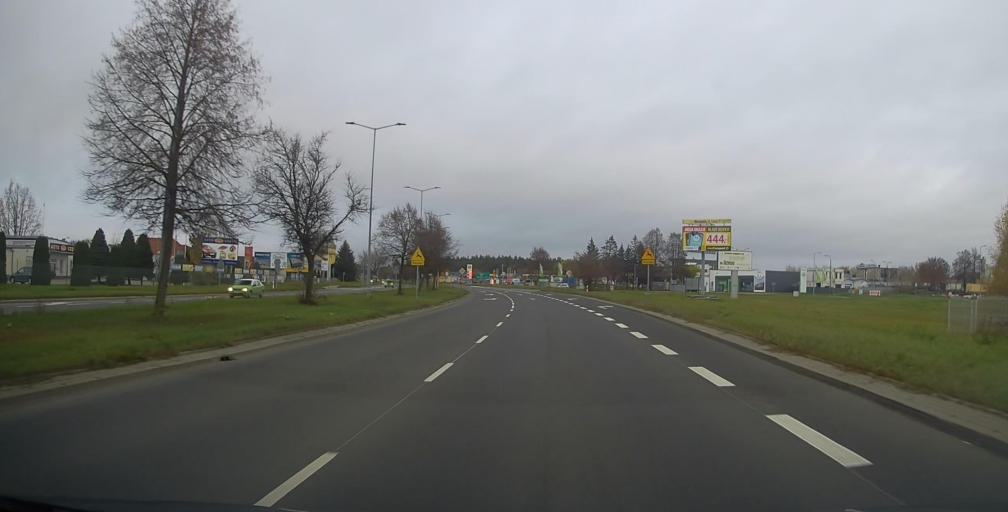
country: PL
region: Warmian-Masurian Voivodeship
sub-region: Powiat elcki
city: Elk
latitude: 53.8298
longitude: 22.3923
